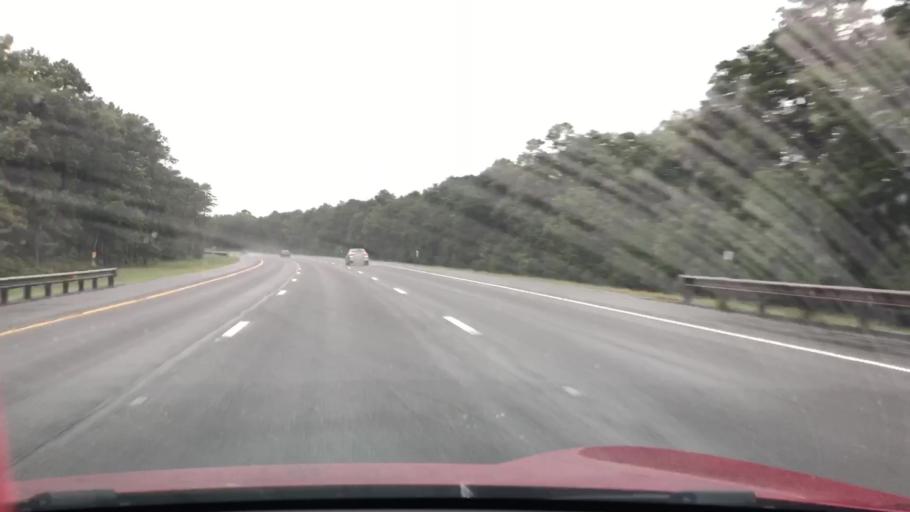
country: US
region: New Jersey
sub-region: Atlantic County
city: Port Republic
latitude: 39.5230
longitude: -74.5137
